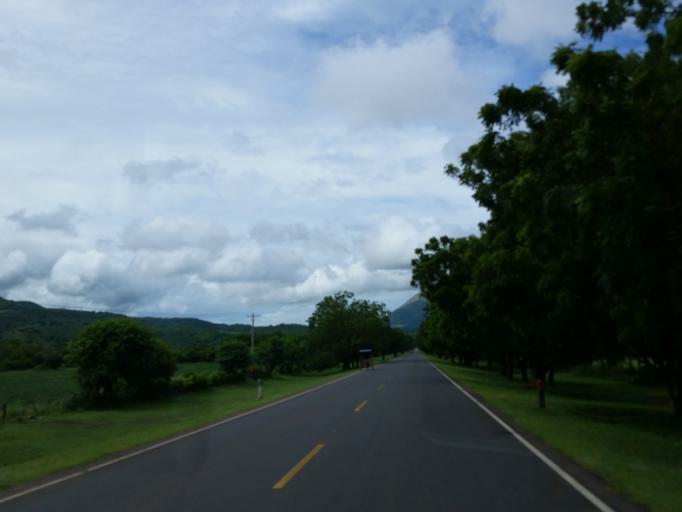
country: NI
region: Leon
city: Telica
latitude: 12.5922
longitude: -86.7269
